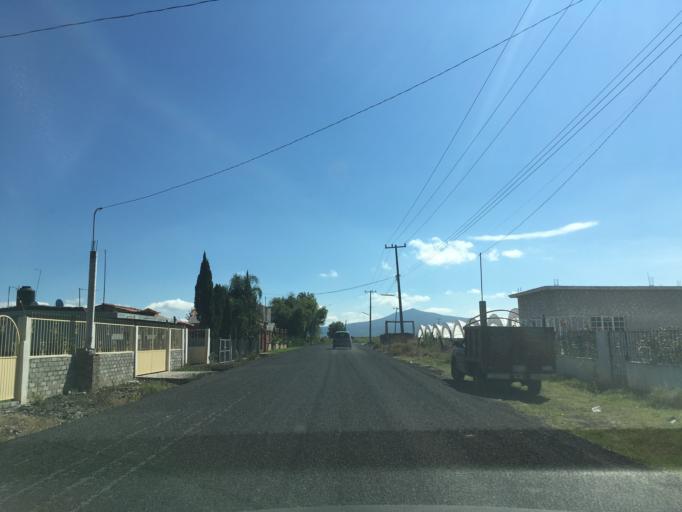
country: MX
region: Mexico
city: Tlazazalca
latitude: 19.9760
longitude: -102.1182
